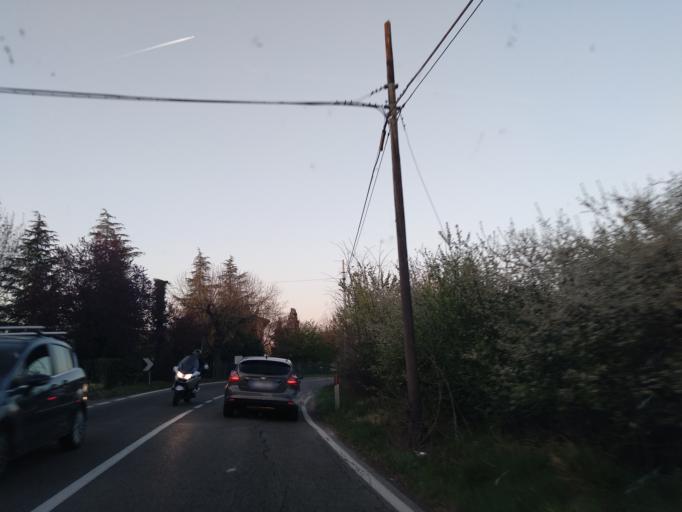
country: IT
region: Emilia-Romagna
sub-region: Provincia di Reggio Emilia
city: Forche
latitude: 44.6414
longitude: 10.5776
